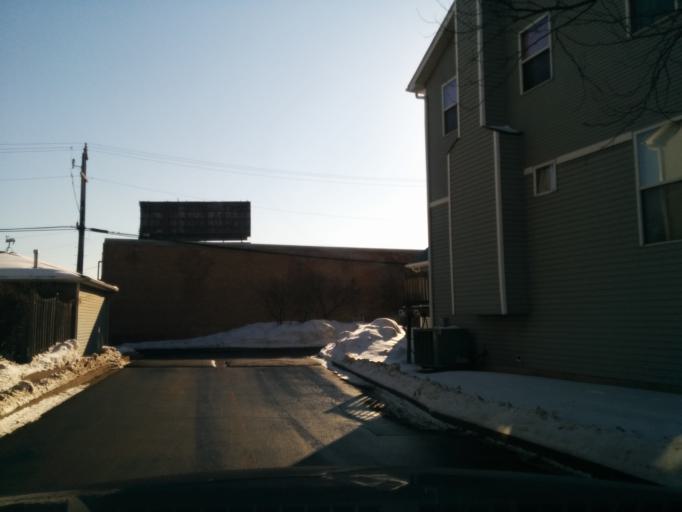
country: US
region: Illinois
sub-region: Cook County
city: Lincolnwood
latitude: 41.9580
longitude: -87.7426
